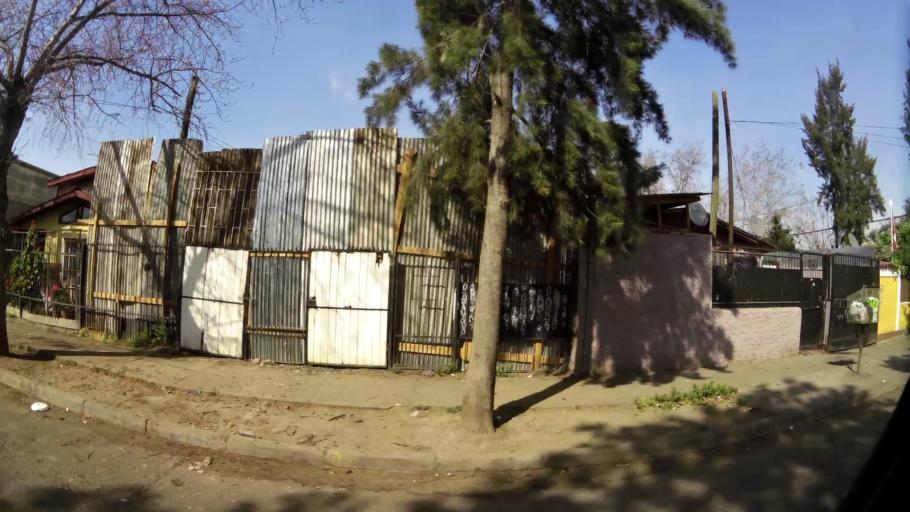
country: CL
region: Santiago Metropolitan
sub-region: Provincia de Santiago
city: Lo Prado
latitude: -33.4262
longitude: -70.7255
